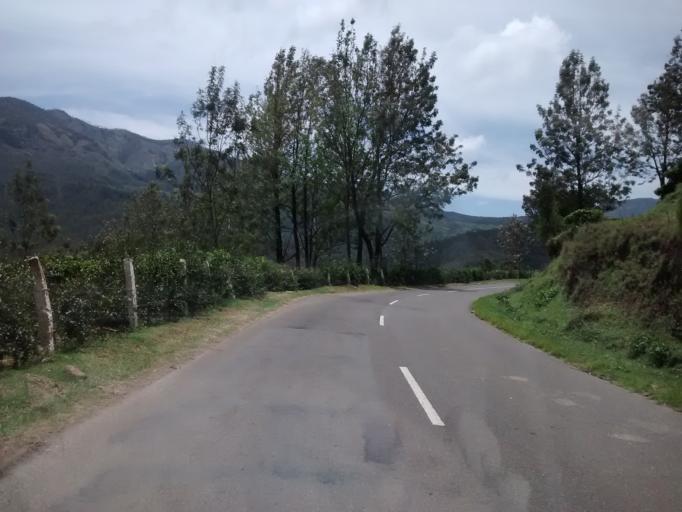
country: IN
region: Kerala
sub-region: Idukki
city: Munnar
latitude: 10.1358
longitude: 77.1805
